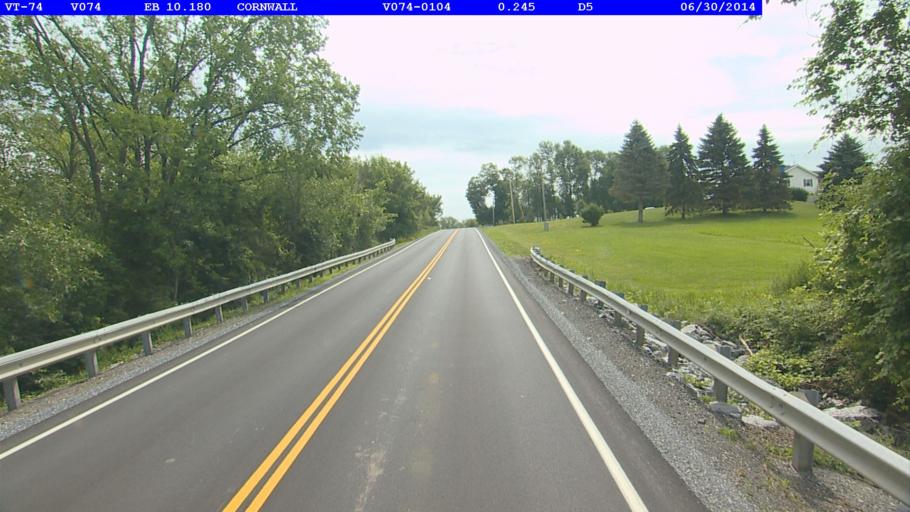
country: US
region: Vermont
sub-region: Addison County
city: Middlebury (village)
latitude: 43.9431
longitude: -73.2527
